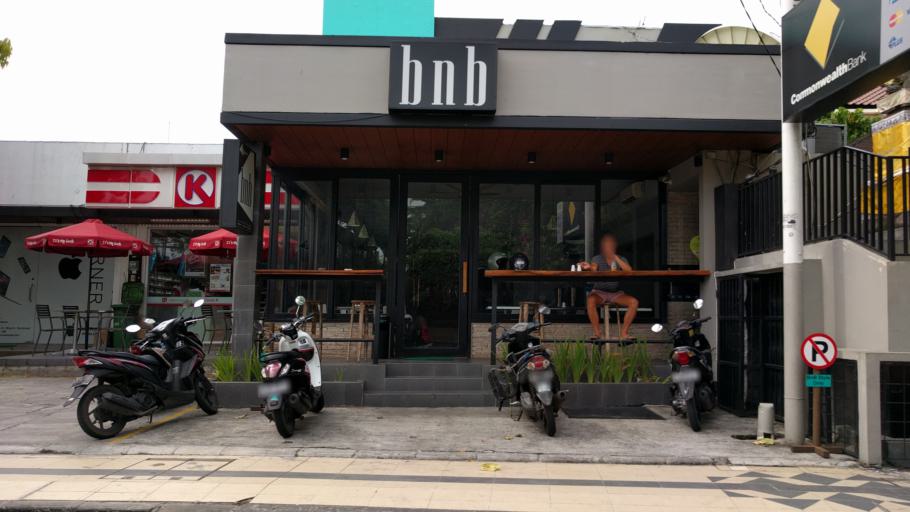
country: ID
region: Bali
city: Kuta
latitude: -8.6885
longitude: 115.1697
